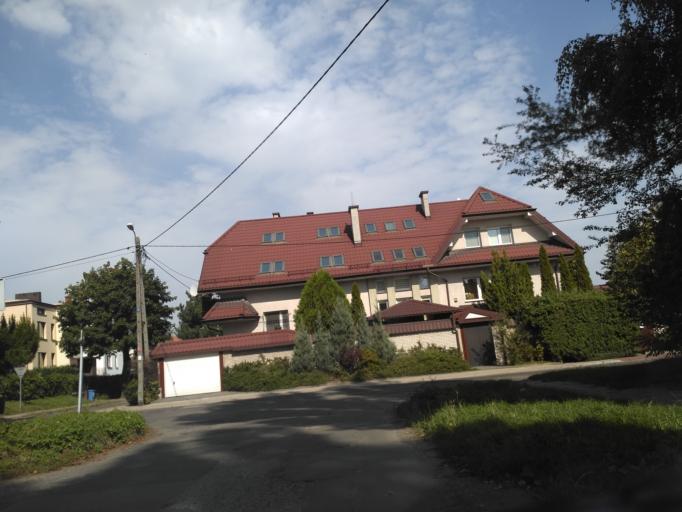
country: PL
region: Lublin Voivodeship
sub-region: Powiat lubelski
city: Lublin
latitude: 51.2104
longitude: 22.5818
